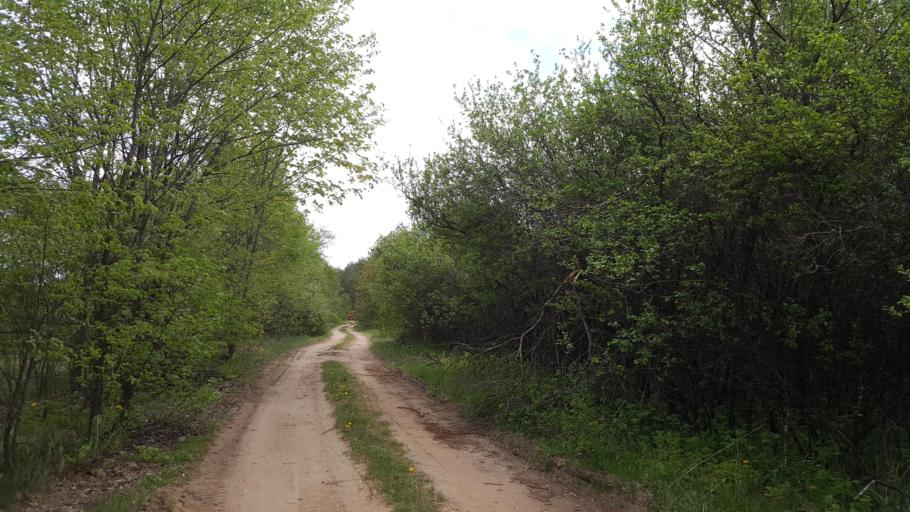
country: BY
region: Brest
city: Zhabinka
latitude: 52.3912
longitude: 24.0425
